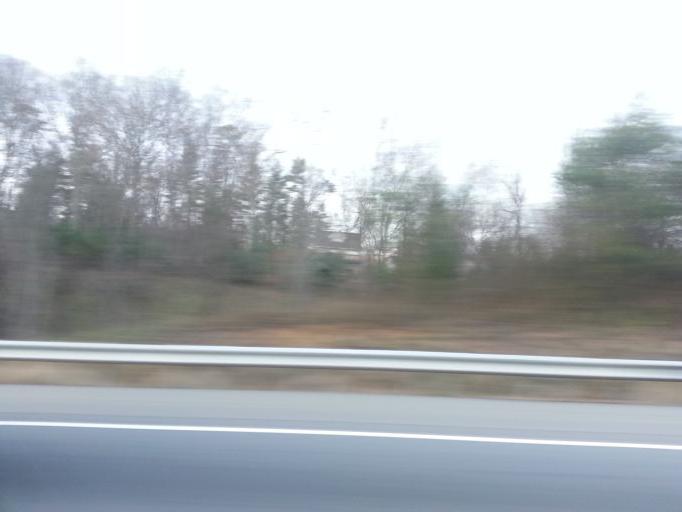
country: US
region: North Carolina
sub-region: Haywood County
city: Canton
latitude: 35.5530
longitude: -82.7253
